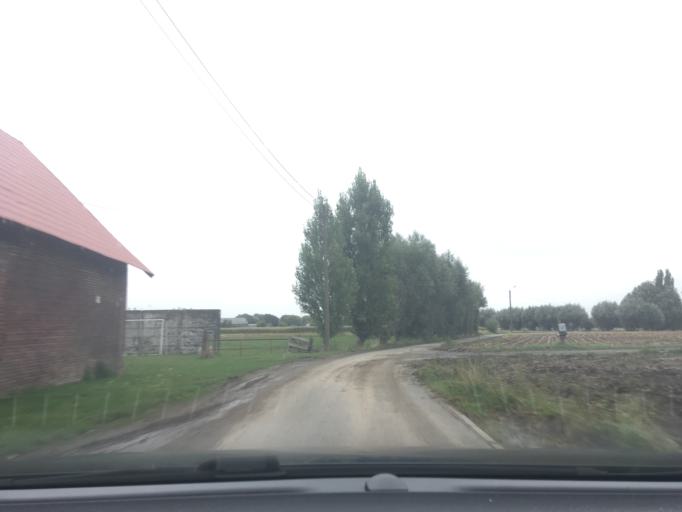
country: BE
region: Flanders
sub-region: Provincie West-Vlaanderen
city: Ledegem
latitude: 50.8943
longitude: 3.1273
